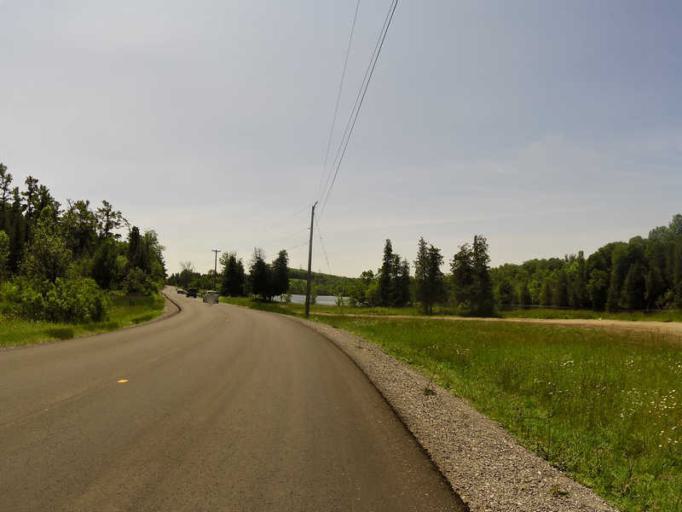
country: CA
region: Ontario
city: Peterborough
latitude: 44.3702
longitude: -78.2904
